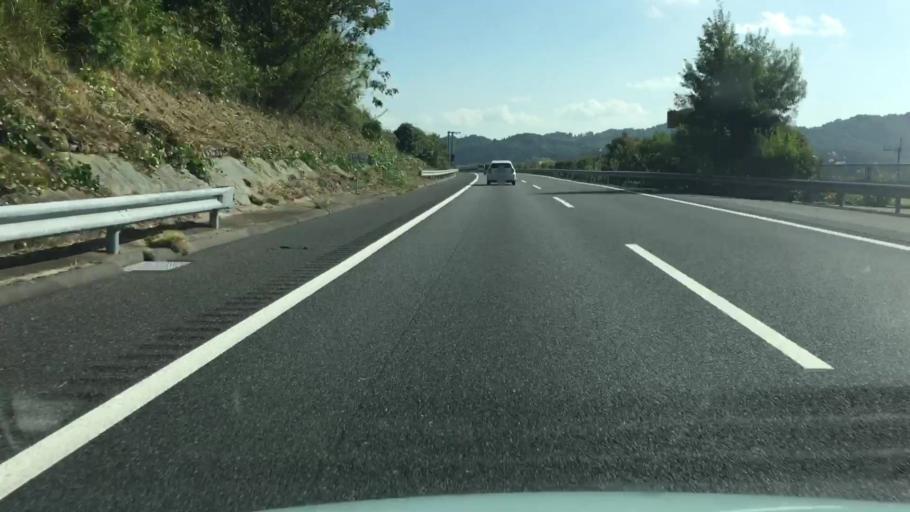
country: JP
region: Ibaraki
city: Iwase
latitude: 36.3423
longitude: 140.1397
